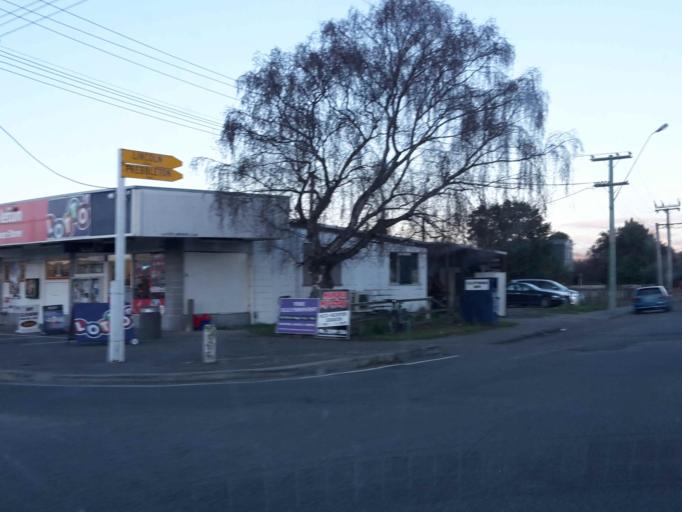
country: NZ
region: Canterbury
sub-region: Selwyn District
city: Prebbleton
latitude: -43.5503
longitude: 172.4868
